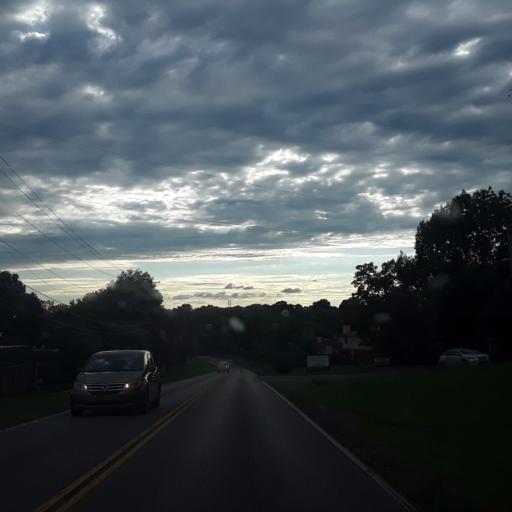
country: US
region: Tennessee
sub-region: Wilson County
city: Green Hill
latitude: 36.1611
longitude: -86.5910
